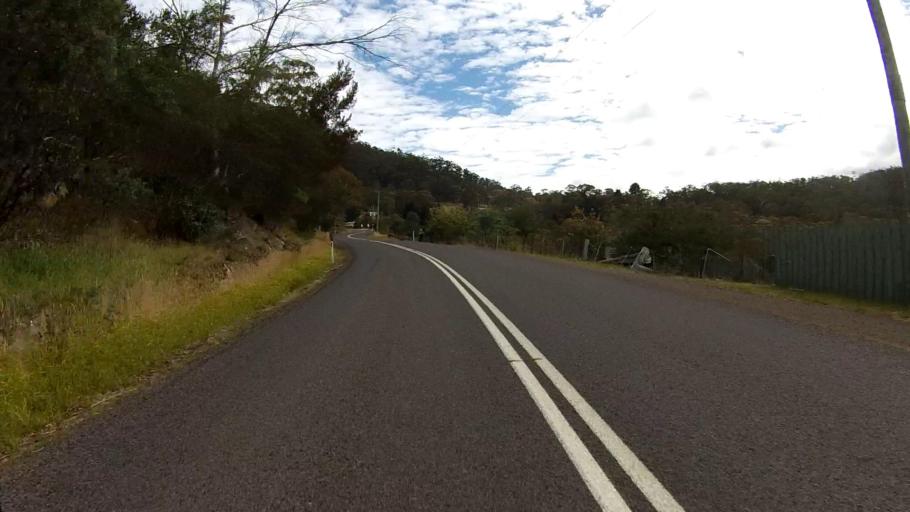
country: AU
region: Tasmania
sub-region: Clarence
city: Lindisfarne
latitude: -42.7867
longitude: 147.3596
